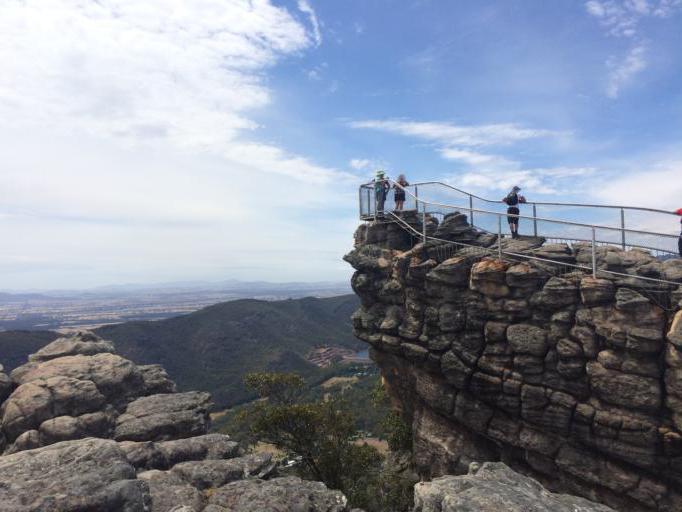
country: AU
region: Victoria
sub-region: Northern Grampians
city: Stawell
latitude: -37.1600
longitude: 142.5156
